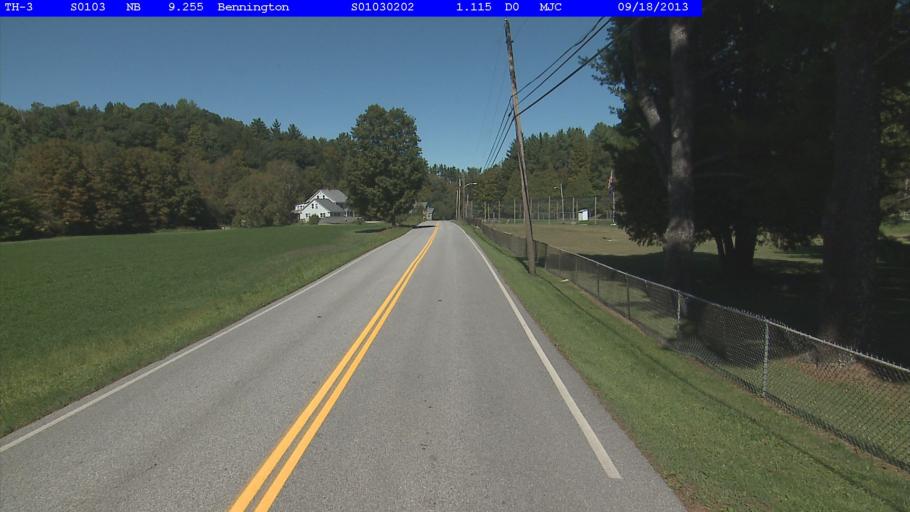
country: US
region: Vermont
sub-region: Bennington County
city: Bennington
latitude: 42.8527
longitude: -73.1735
